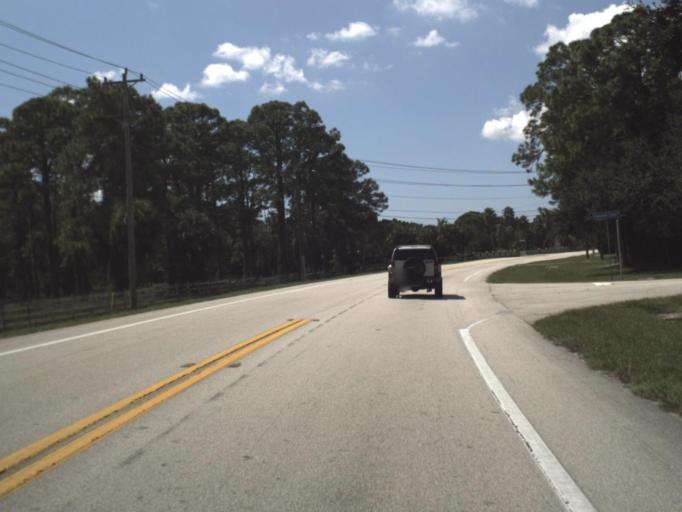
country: US
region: Florida
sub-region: Lee County
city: Fort Myers Shores
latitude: 26.7152
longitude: -81.7714
